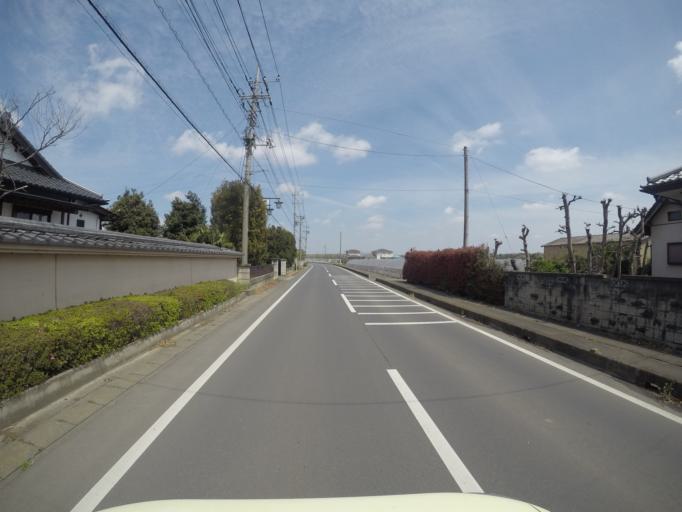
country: JP
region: Ibaraki
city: Shimodate
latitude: 36.2956
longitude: 140.0282
